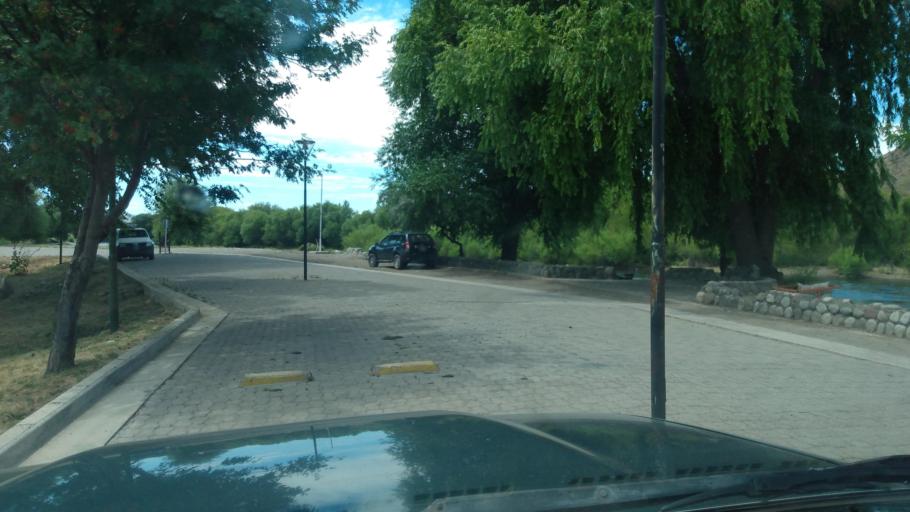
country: AR
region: Neuquen
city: Junin de los Andes
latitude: -39.9467
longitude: -71.0647
